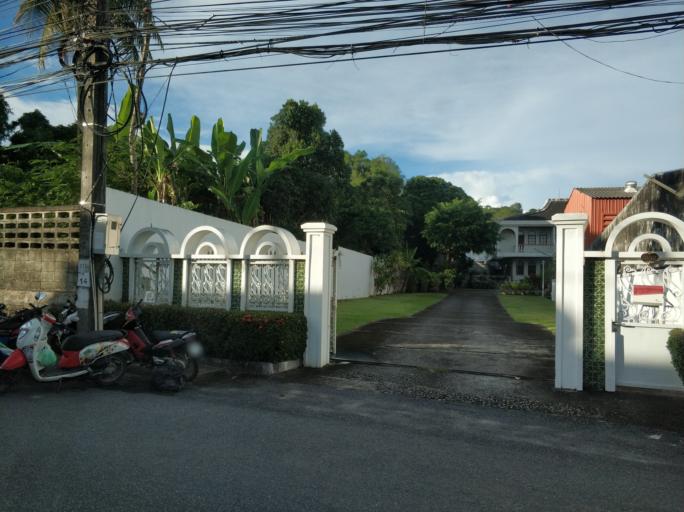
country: TH
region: Phuket
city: Ban Talat Nua
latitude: 7.8851
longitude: 98.3787
